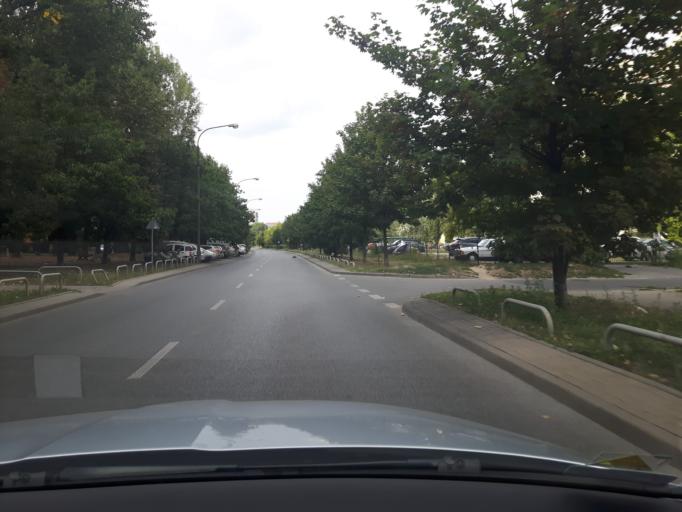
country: PL
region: Masovian Voivodeship
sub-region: Warszawa
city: Mokotow
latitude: 52.1758
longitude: 21.0131
